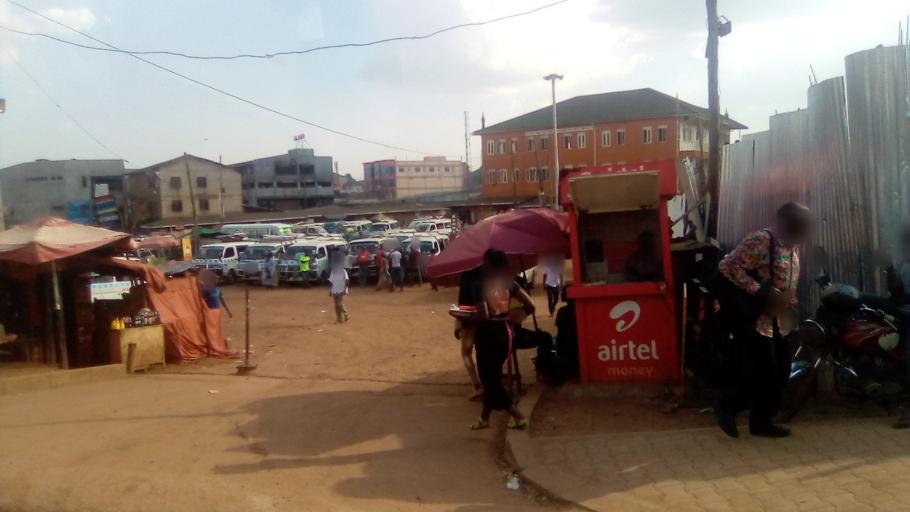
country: UG
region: Central Region
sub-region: Kampala District
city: Kampala
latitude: 0.3113
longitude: 32.5715
